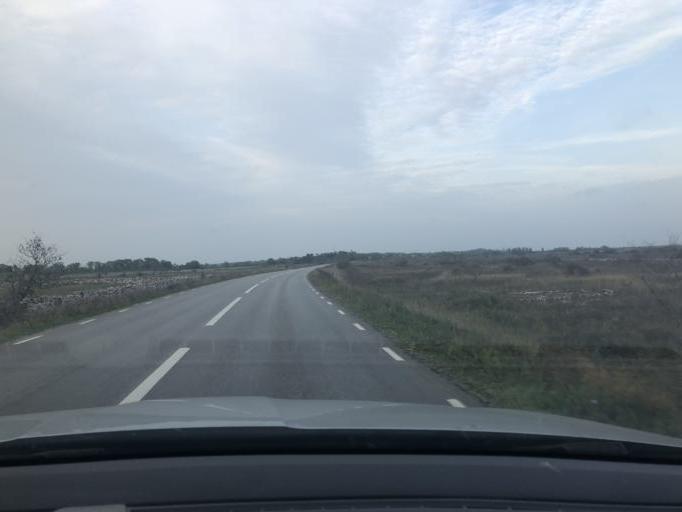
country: SE
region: Kalmar
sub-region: Morbylanga Kommun
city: Moerbylanga
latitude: 56.4984
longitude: 16.4267
